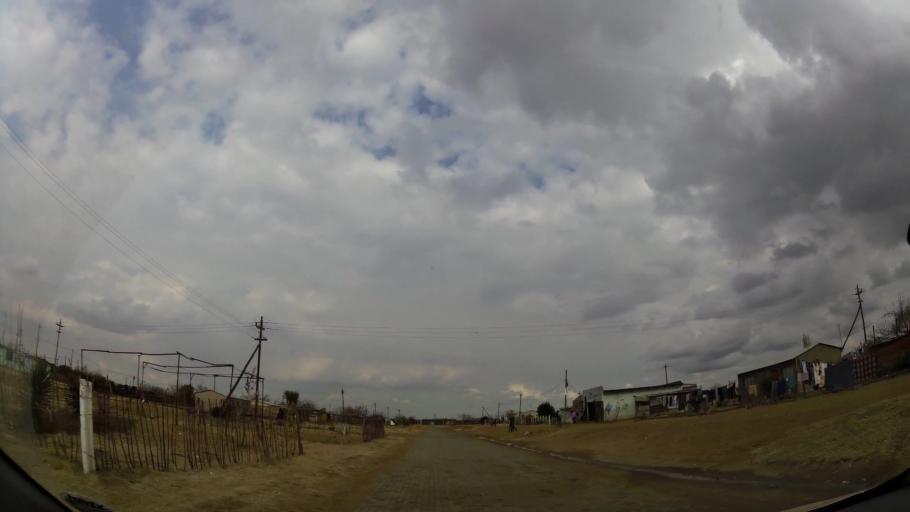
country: ZA
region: Orange Free State
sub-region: Fezile Dabi District Municipality
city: Sasolburg
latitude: -26.8803
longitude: 27.8808
